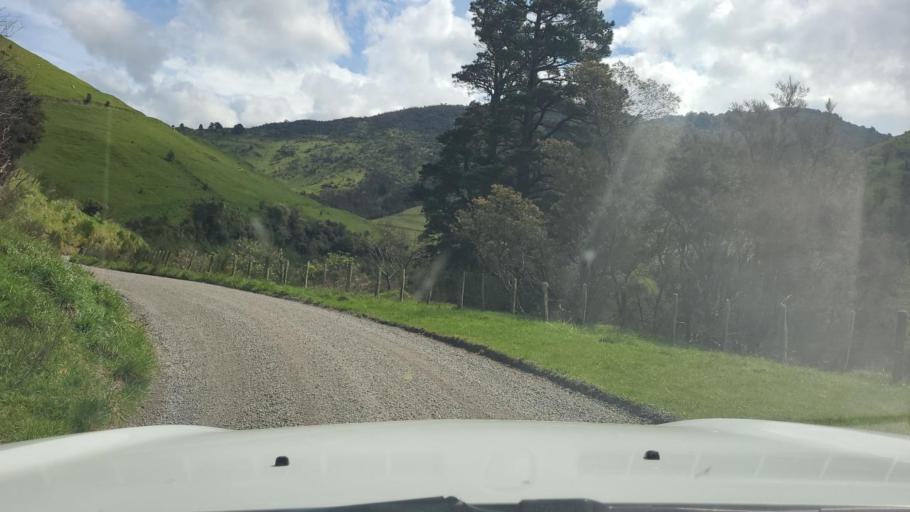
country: NZ
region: Wellington
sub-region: Masterton District
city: Masterton
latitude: -40.9315
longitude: 175.4969
